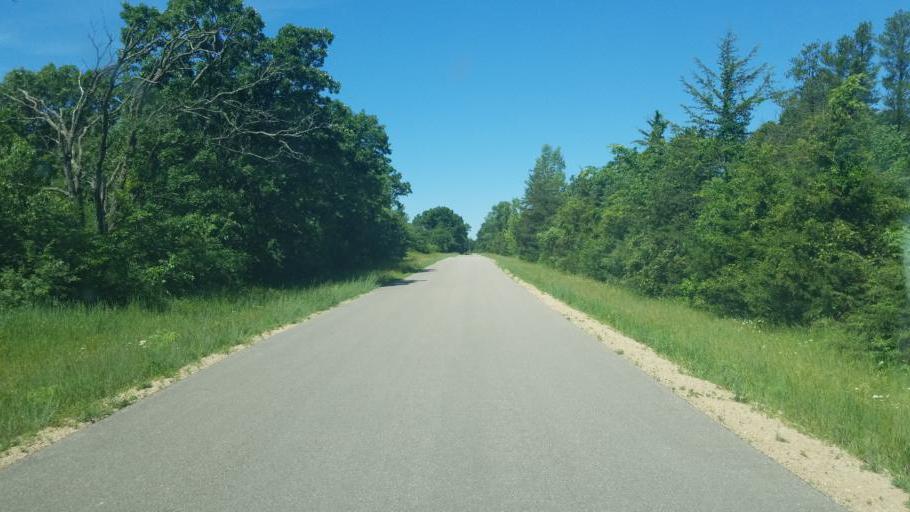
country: US
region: Wisconsin
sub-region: Adams County
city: Adams
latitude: 43.8695
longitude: -89.9389
